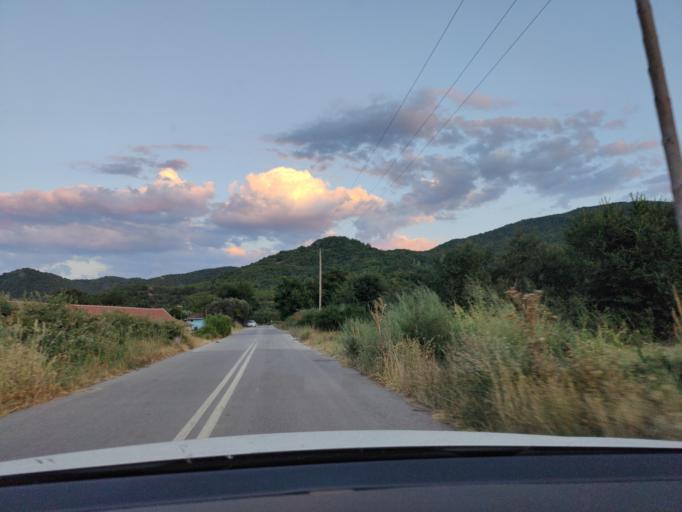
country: GR
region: Central Macedonia
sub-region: Nomos Serron
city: Chrysochorafa
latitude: 41.1780
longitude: 23.1130
